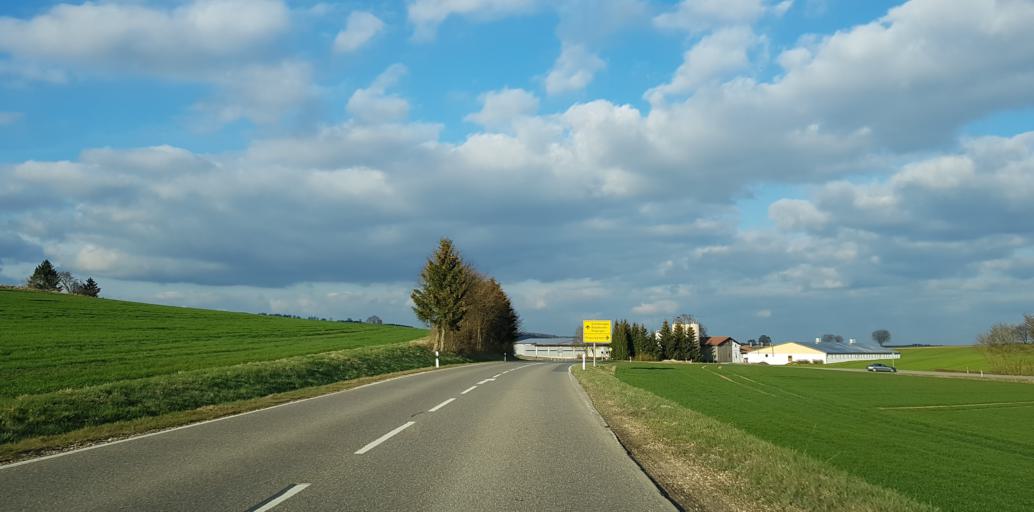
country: DE
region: Baden-Wuerttemberg
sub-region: Tuebingen Region
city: Altheim
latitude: 48.3340
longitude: 9.8046
